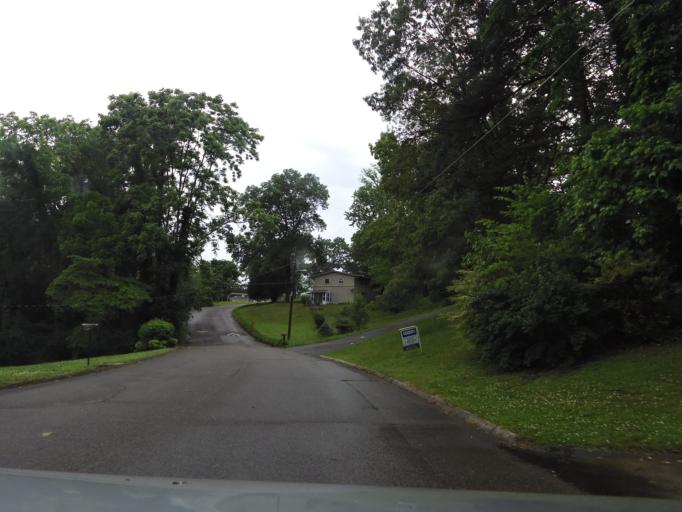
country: US
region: Tennessee
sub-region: Knox County
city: Knoxville
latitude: 36.0037
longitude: -83.8961
